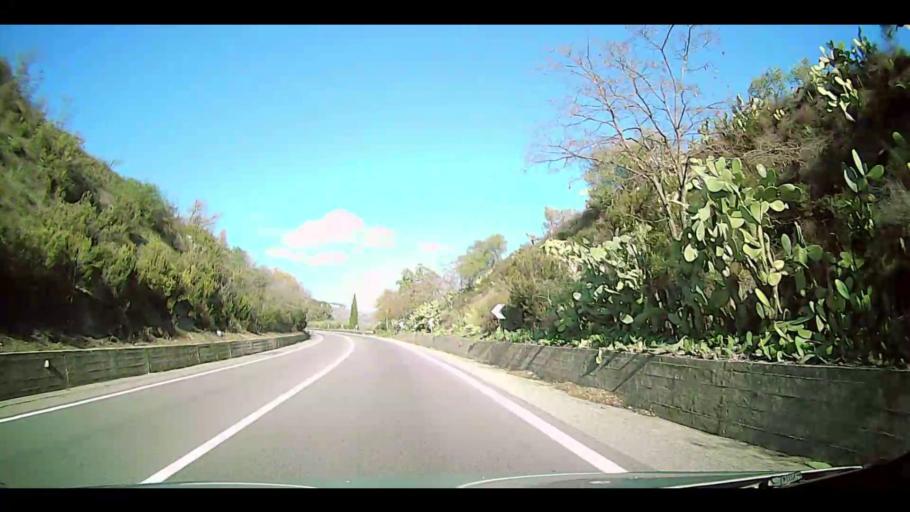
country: IT
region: Calabria
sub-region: Provincia di Crotone
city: Caccuri
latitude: 39.2012
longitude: 16.8113
